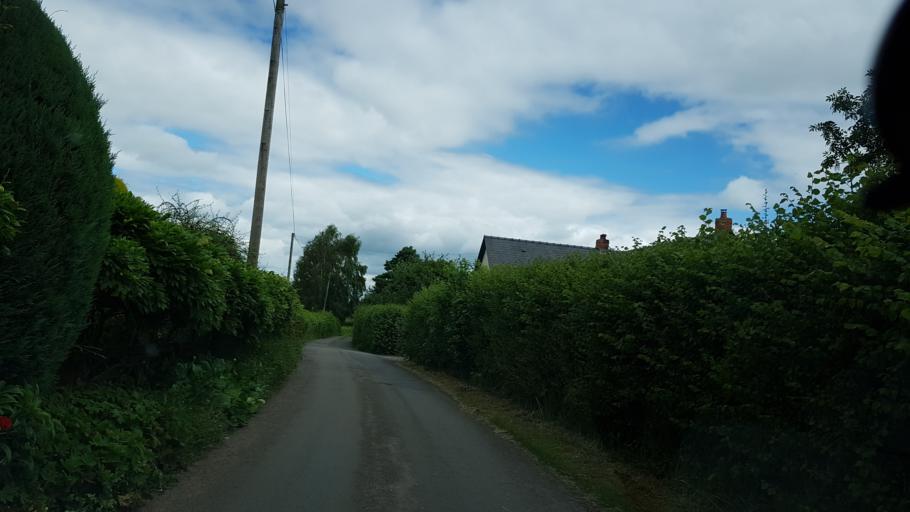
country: GB
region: Wales
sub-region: Monmouthshire
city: Llanarth
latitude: 51.7935
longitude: -2.8262
